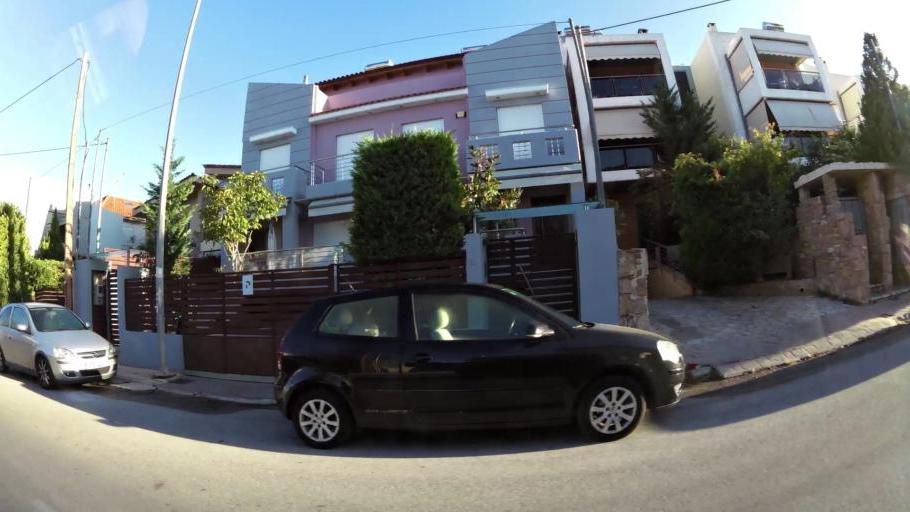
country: GR
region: Attica
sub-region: Nomarchia Anatolikis Attikis
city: Gerakas
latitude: 38.0257
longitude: 23.8446
